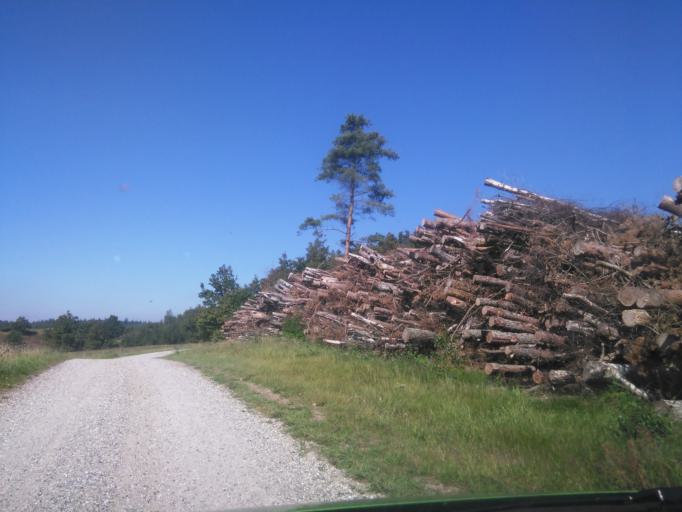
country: DK
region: Central Jutland
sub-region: Syddjurs Kommune
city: Ronde
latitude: 56.2102
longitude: 10.5333
